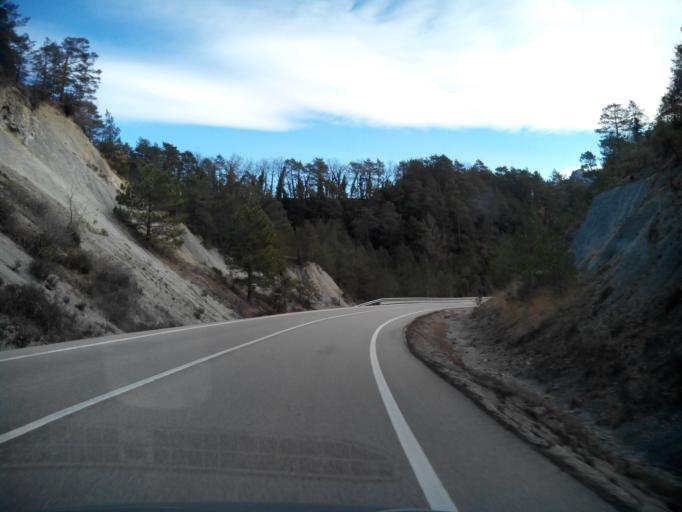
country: ES
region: Catalonia
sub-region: Provincia de Barcelona
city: Vilada
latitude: 42.1297
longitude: 1.9082
